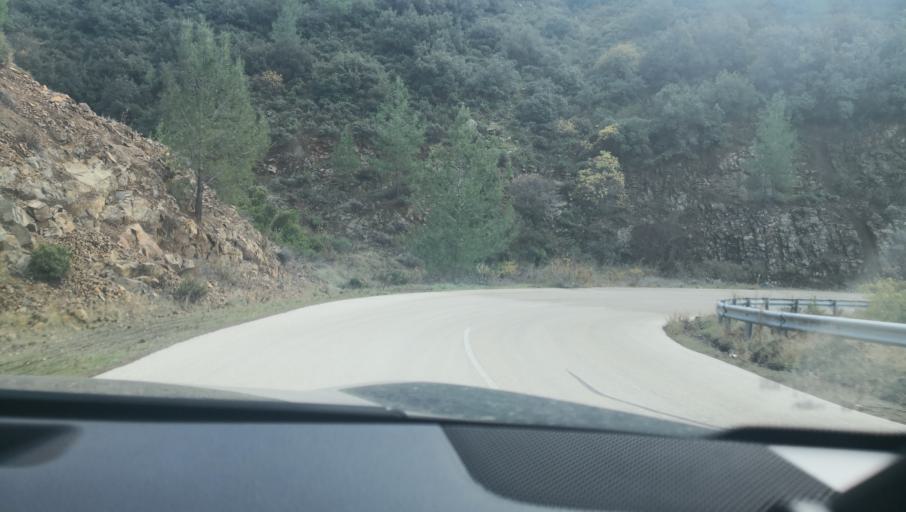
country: CY
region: Lefkosia
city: Lefka
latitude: 35.0535
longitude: 32.7485
